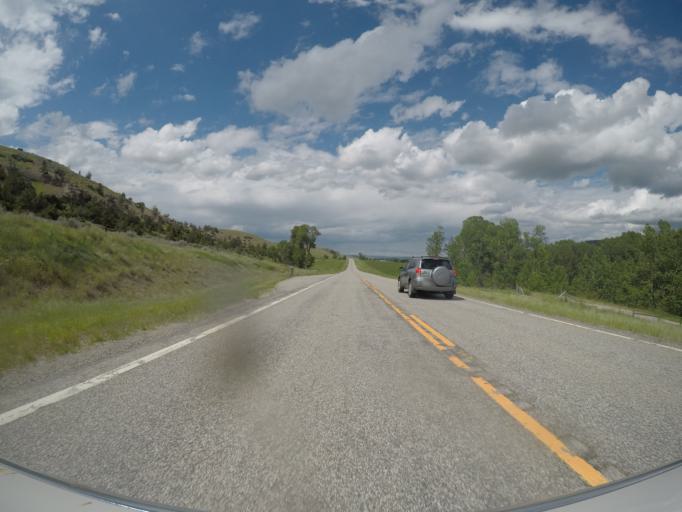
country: US
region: Montana
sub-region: Sweet Grass County
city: Big Timber
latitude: 45.7404
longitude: -109.9972
